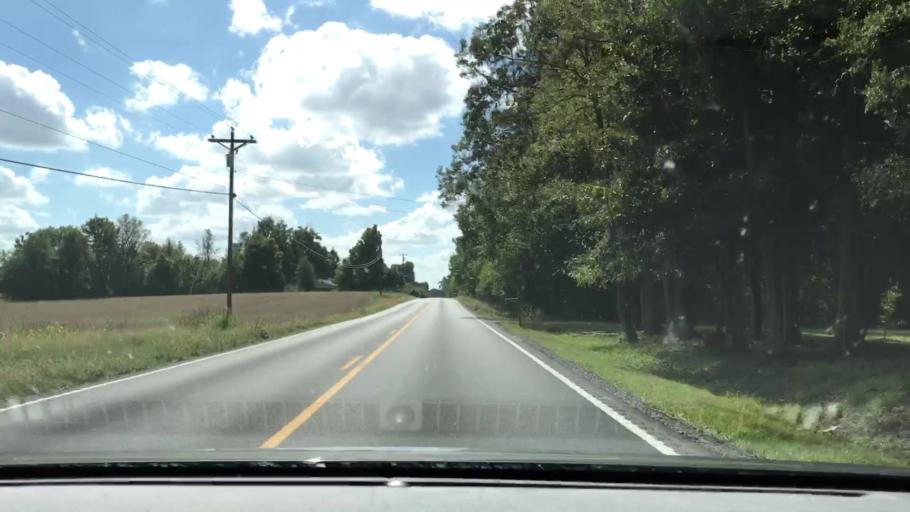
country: US
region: Kentucky
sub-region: Graves County
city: Mayfield
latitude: 36.7971
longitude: -88.5955
